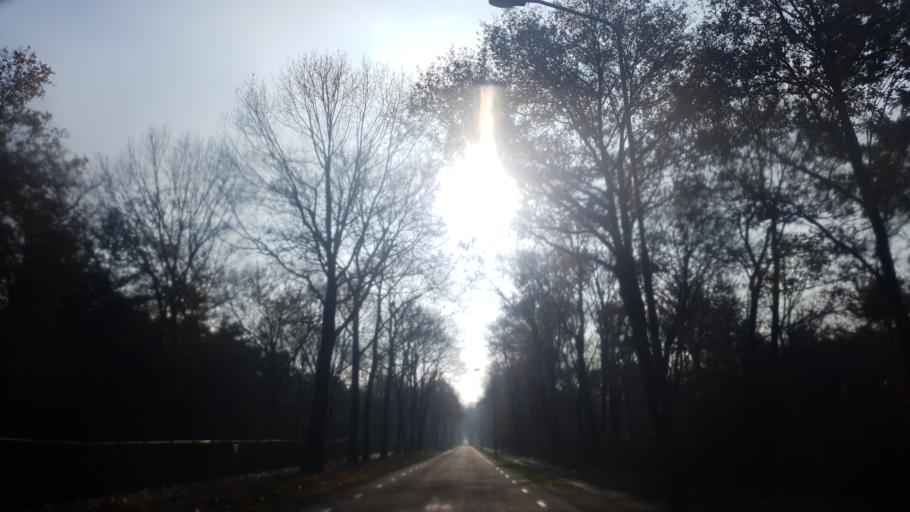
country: NL
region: North Brabant
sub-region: Gemeente Landerd
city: Reek
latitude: 51.7298
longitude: 5.6822
